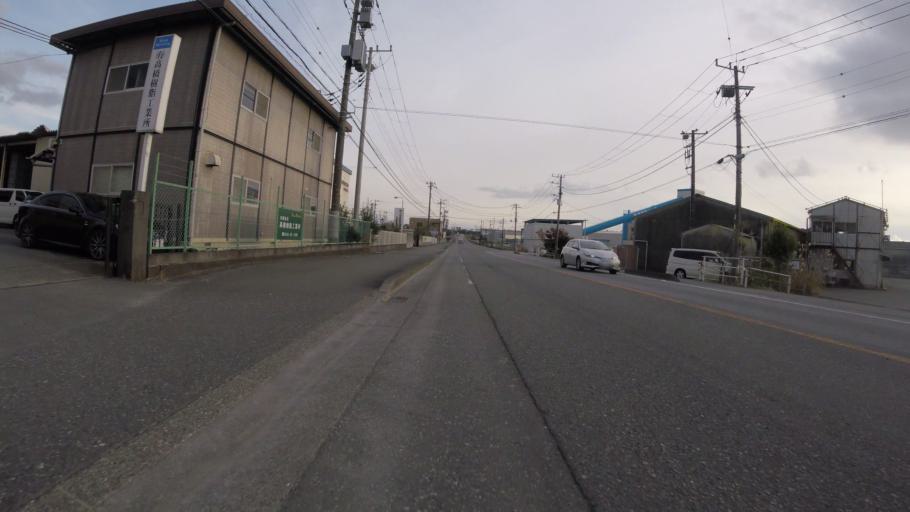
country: JP
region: Shizuoka
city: Fuji
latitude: 35.1440
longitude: 138.7201
